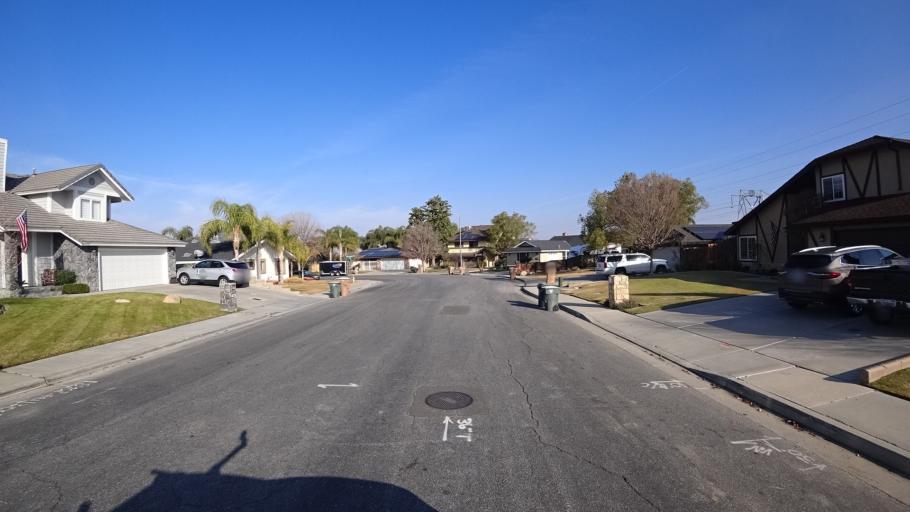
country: US
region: California
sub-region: Kern County
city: Oildale
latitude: 35.4045
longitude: -118.9236
